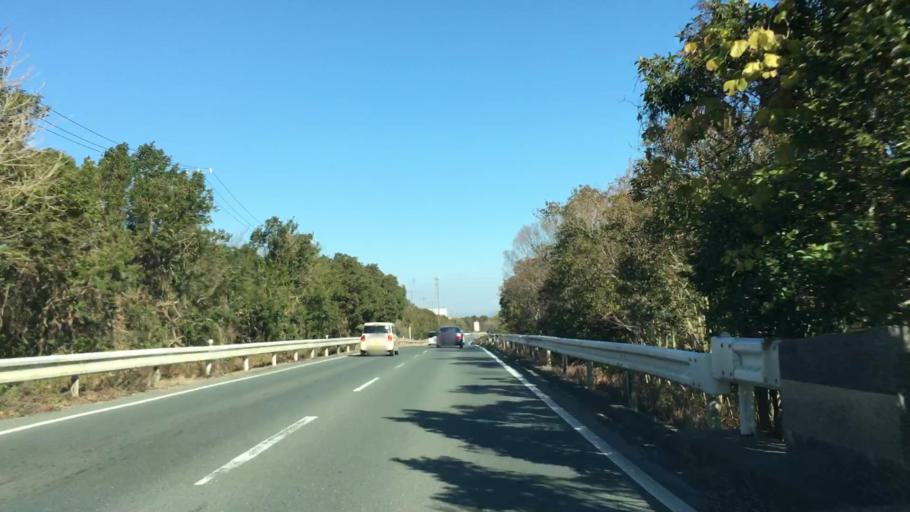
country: JP
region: Aichi
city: Tahara
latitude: 34.7025
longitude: 137.3273
